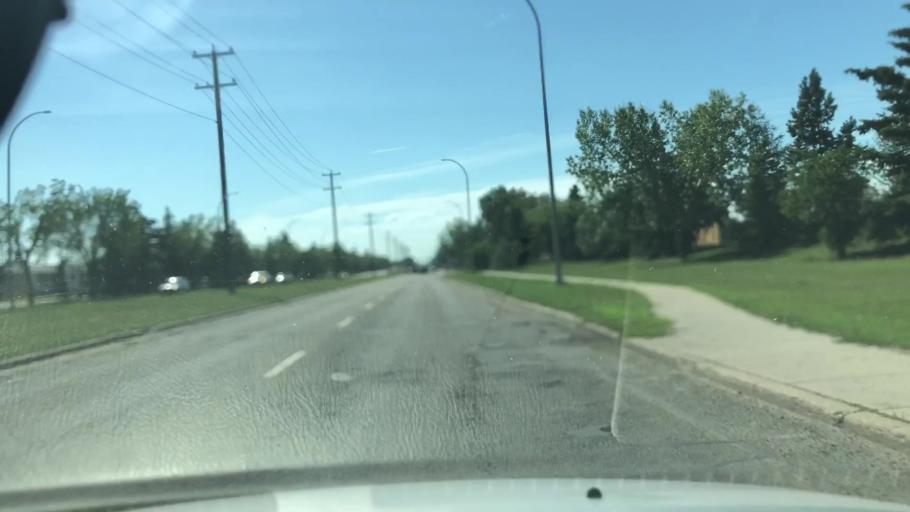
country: CA
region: Alberta
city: Edmonton
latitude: 53.5996
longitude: -113.5274
